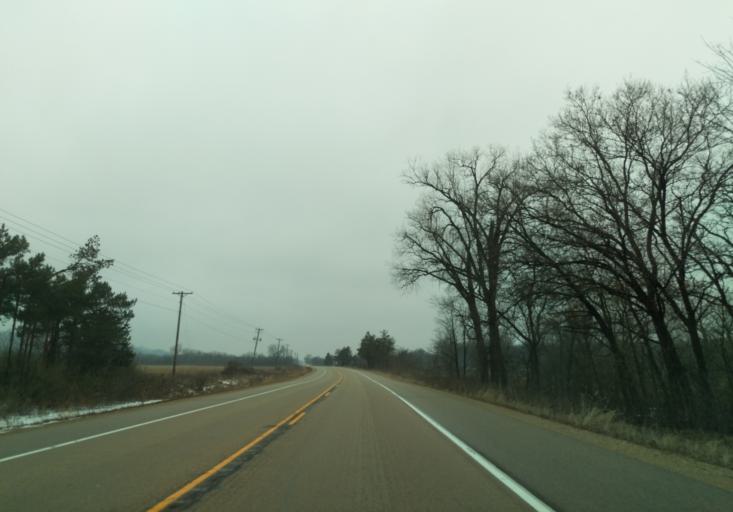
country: US
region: Wisconsin
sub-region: Dane County
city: Mazomanie
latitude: 43.1618
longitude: -89.8574
